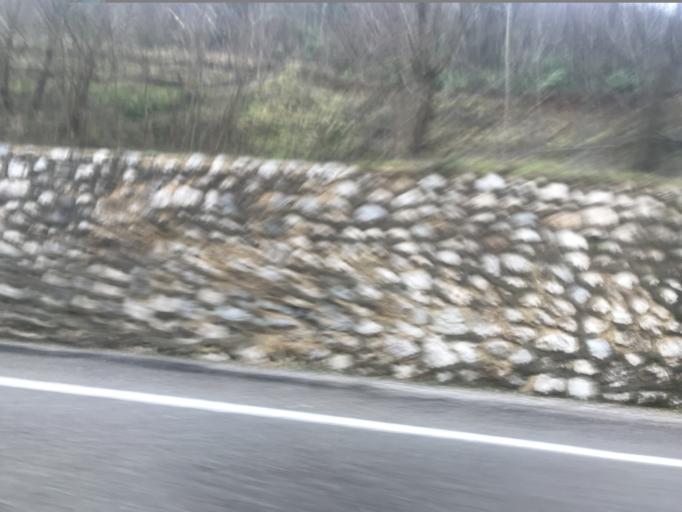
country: TR
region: Bartin
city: Amasra
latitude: 41.7007
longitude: 32.3840
